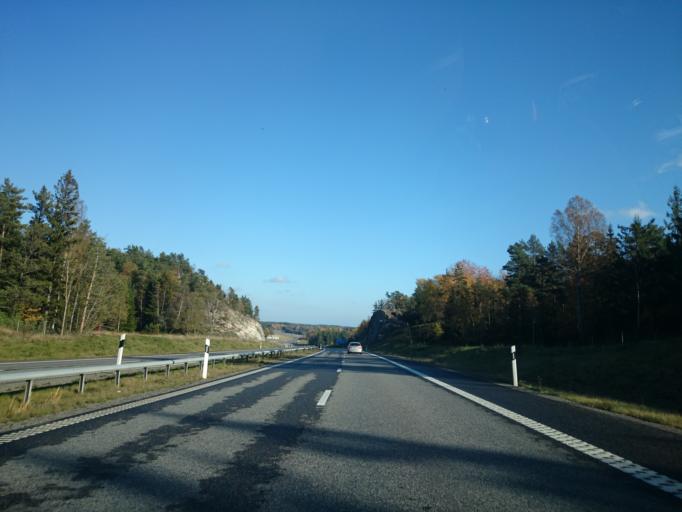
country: SE
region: Stockholm
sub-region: Haninge Kommun
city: Jordbro
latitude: 59.0601
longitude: 18.0281
